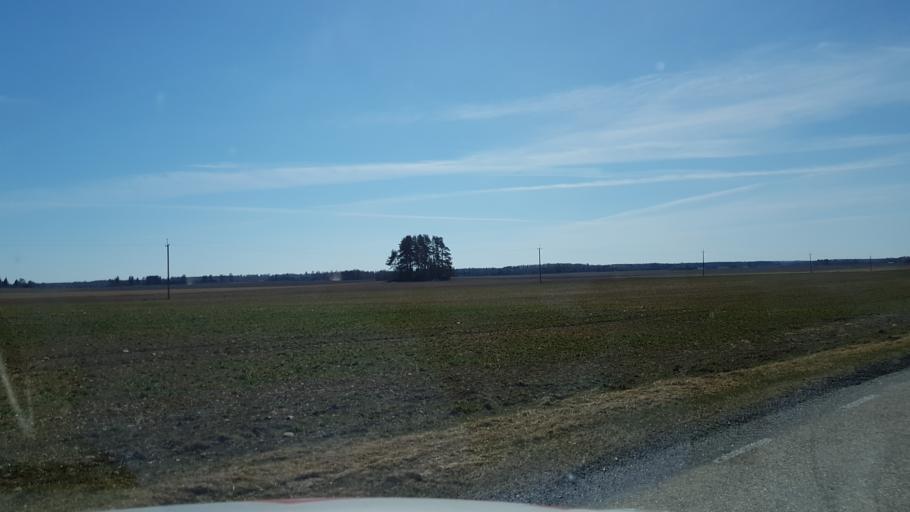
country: EE
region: Laeaene-Virumaa
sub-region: Vinni vald
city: Vinni
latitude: 59.0850
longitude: 26.4624
